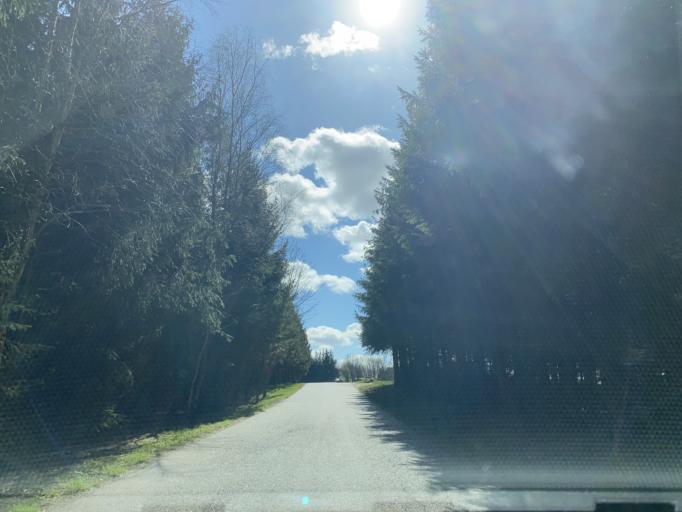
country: DK
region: Central Jutland
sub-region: Favrskov Kommune
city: Ulstrup
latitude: 56.3333
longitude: 9.7876
